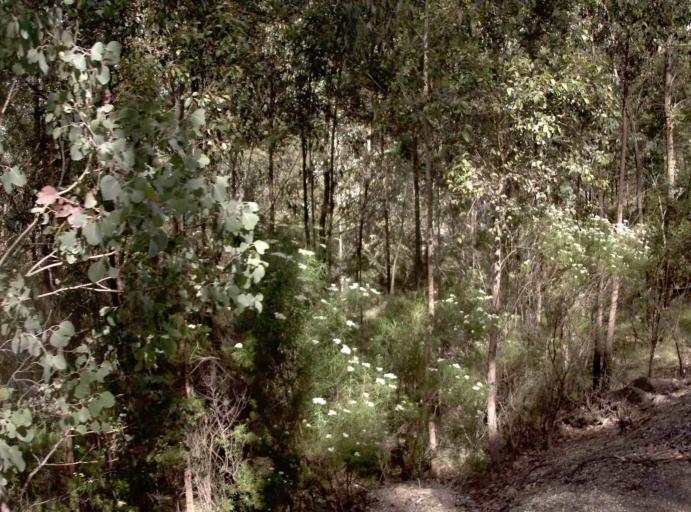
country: AU
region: Victoria
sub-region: East Gippsland
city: Lakes Entrance
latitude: -37.4733
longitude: 148.1245
